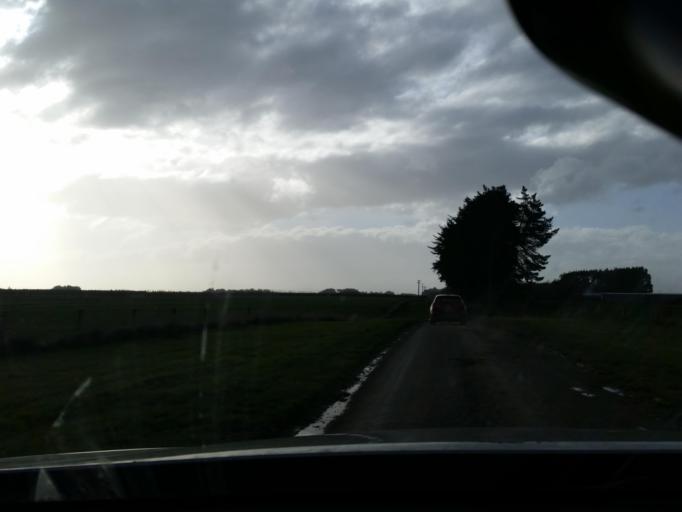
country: NZ
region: Southland
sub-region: Southland District
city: Winton
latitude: -46.2474
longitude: 168.3222
